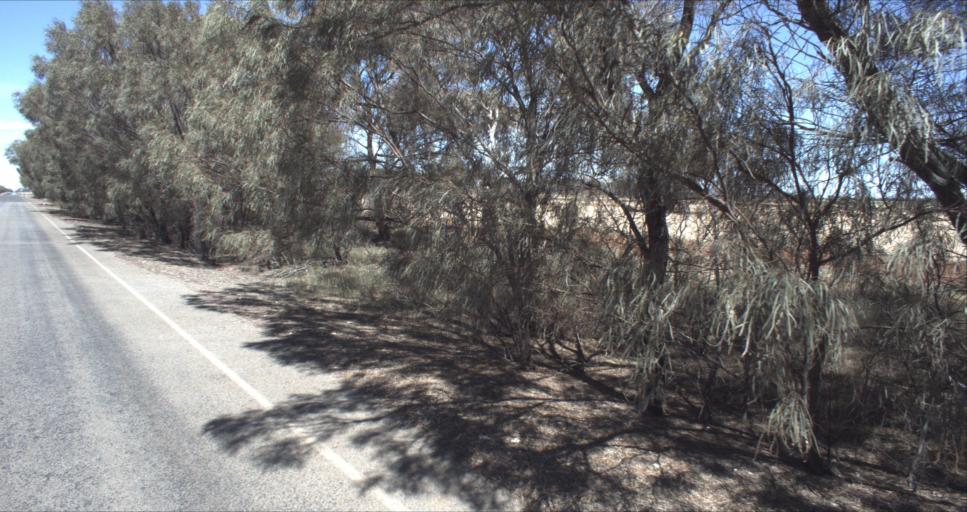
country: AU
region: New South Wales
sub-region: Leeton
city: Leeton
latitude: -34.4706
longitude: 146.2924
